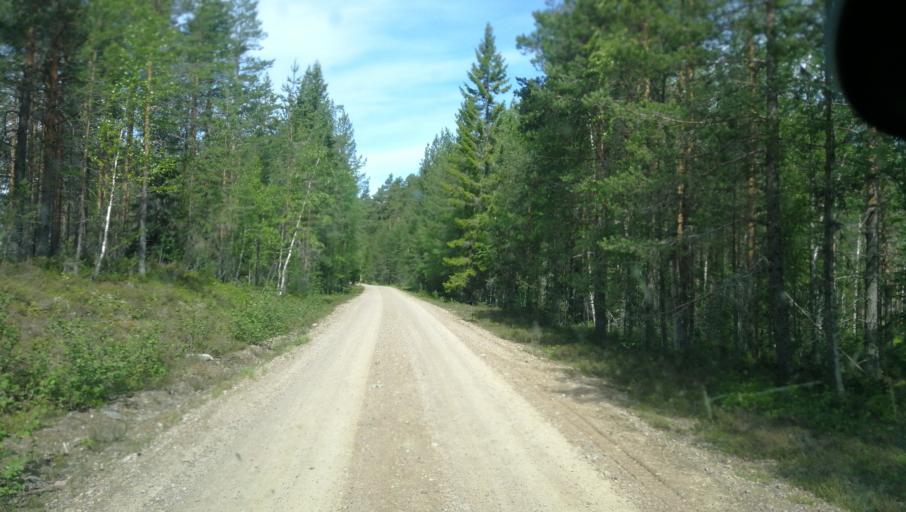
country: SE
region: Dalarna
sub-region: Vansbro Kommun
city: Vansbro
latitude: 60.8182
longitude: 14.1851
